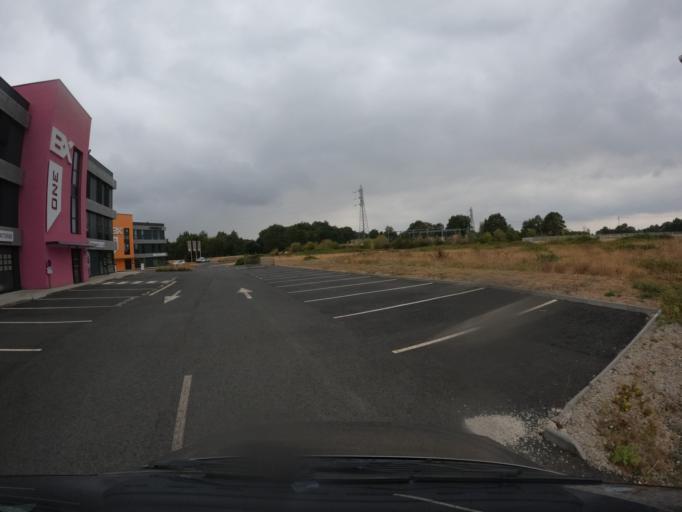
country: FR
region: Pays de la Loire
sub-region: Departement de la Vendee
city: Bouffere
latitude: 46.9754
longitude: -1.3368
